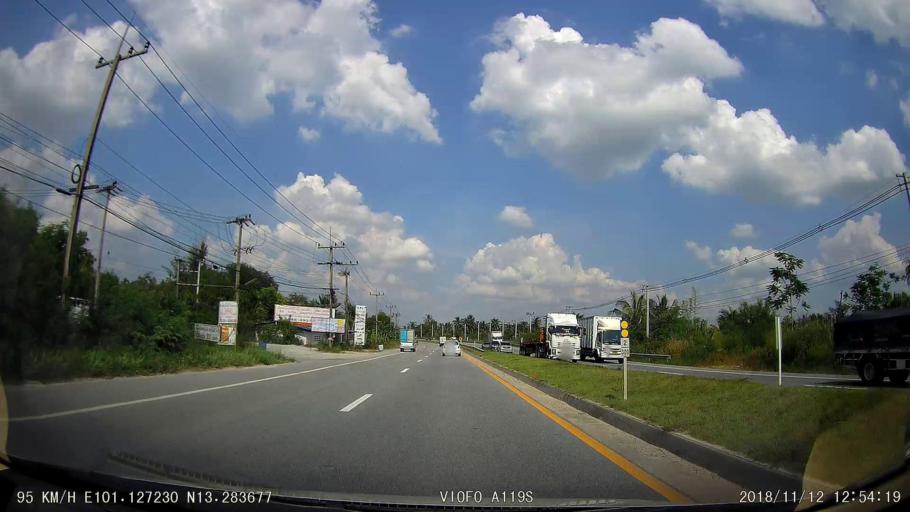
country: TH
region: Chon Buri
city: Ban Bueng
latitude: 13.2839
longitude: 101.1274
